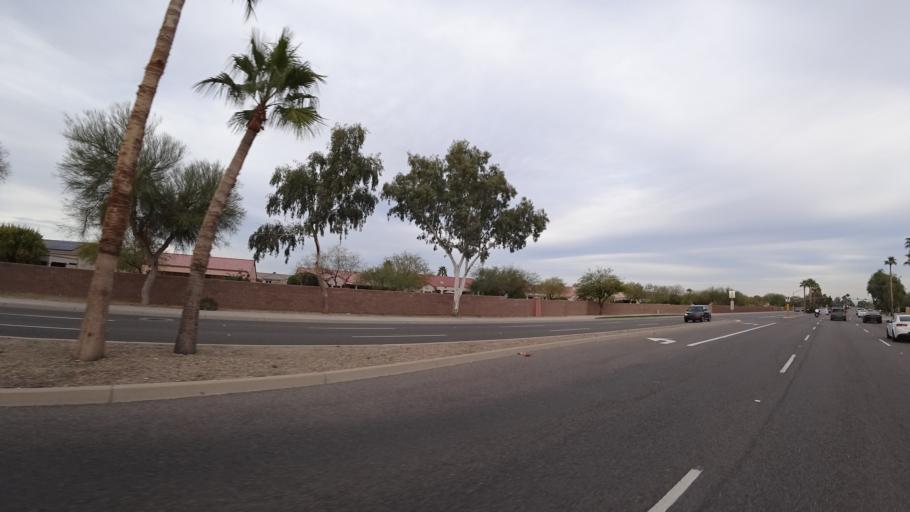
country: US
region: Arizona
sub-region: Maricopa County
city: Sun City West
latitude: 33.6387
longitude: -112.4122
